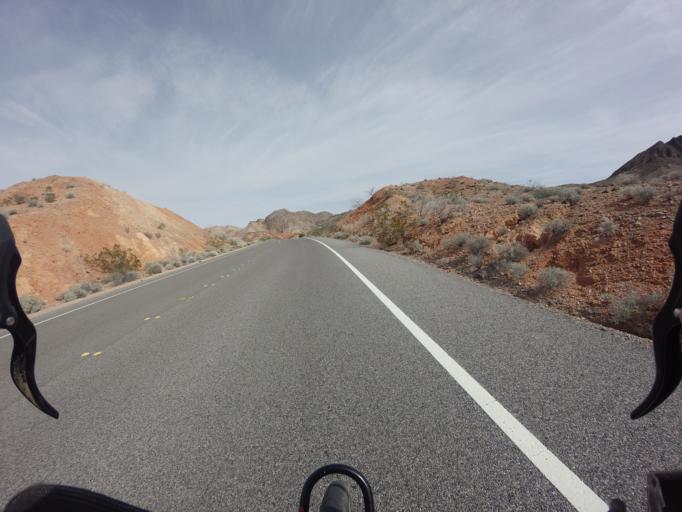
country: US
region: Nevada
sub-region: Clark County
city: Boulder City
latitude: 36.1907
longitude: -114.7353
